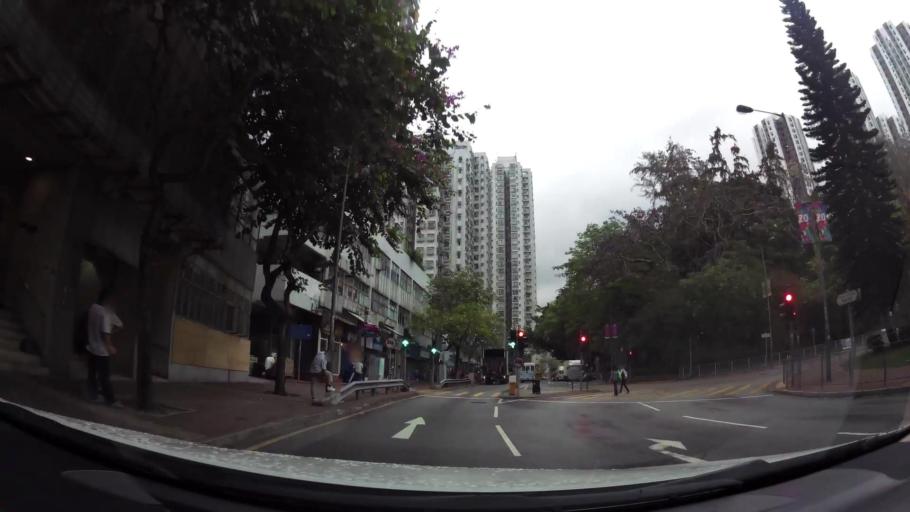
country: HK
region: Tsuen Wan
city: Tsuen Wan
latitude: 22.3708
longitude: 114.1207
